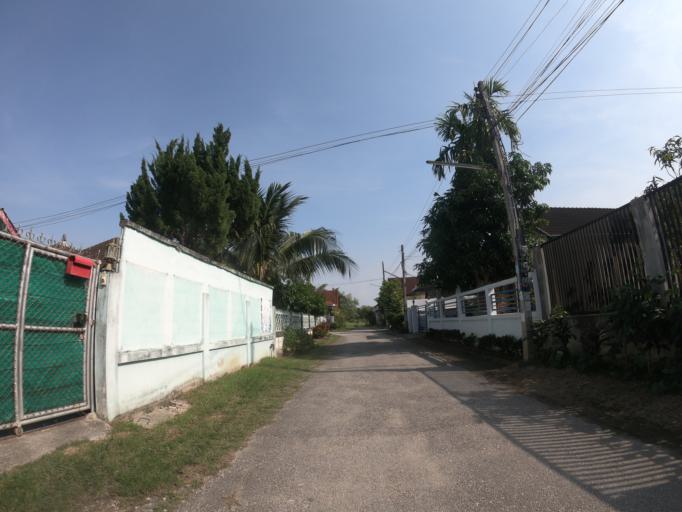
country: TH
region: Chiang Mai
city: Chiang Mai
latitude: 18.7692
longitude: 99.0154
